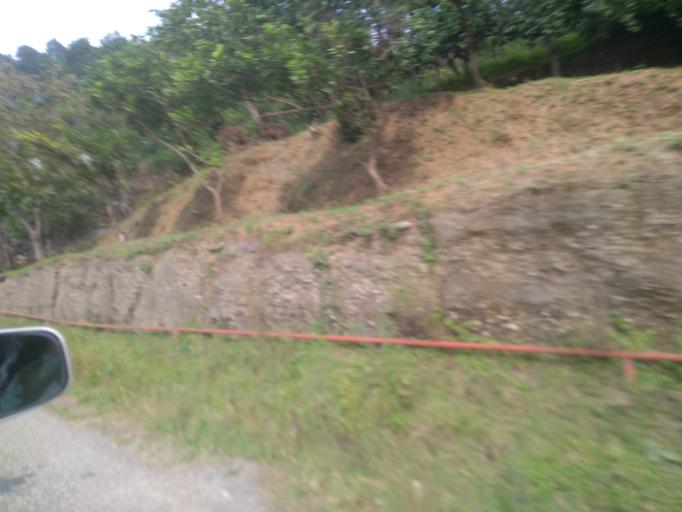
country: GE
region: Ajaria
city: Khelvachauri
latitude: 41.5619
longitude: 41.6932
